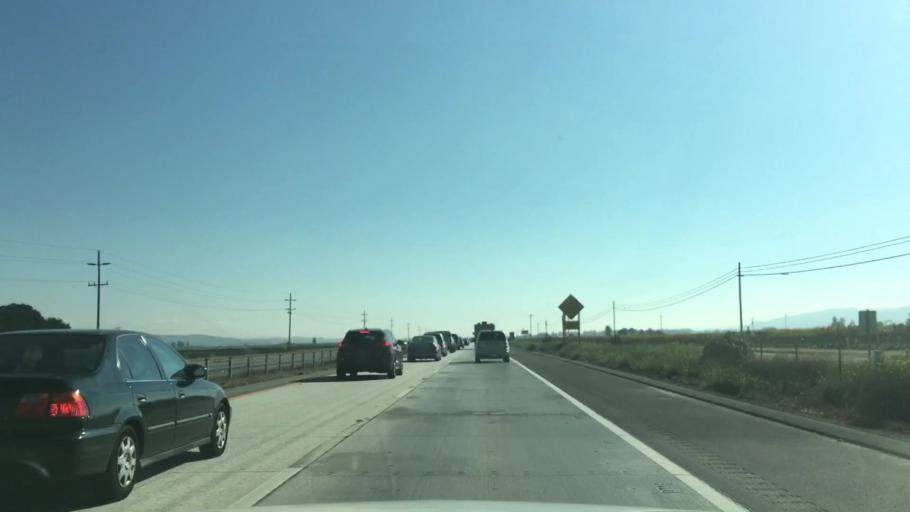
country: US
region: California
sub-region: Monterey County
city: Soledad
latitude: 36.3825
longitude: -121.2999
